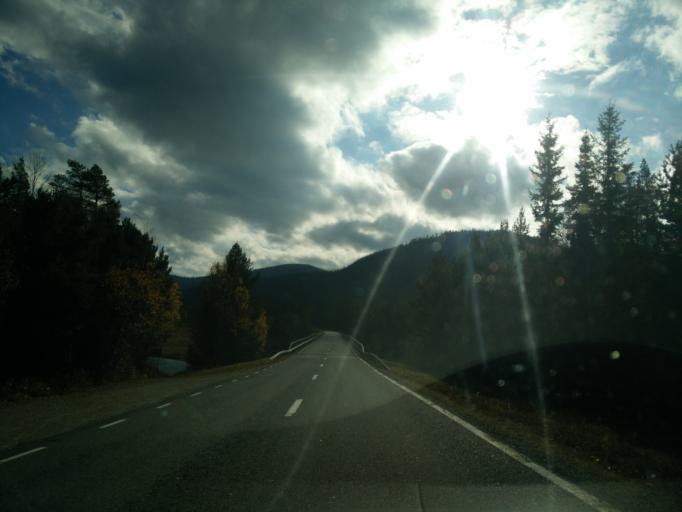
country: NO
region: Hedmark
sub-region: Engerdal
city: Engerdal
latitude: 62.4341
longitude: 12.7141
